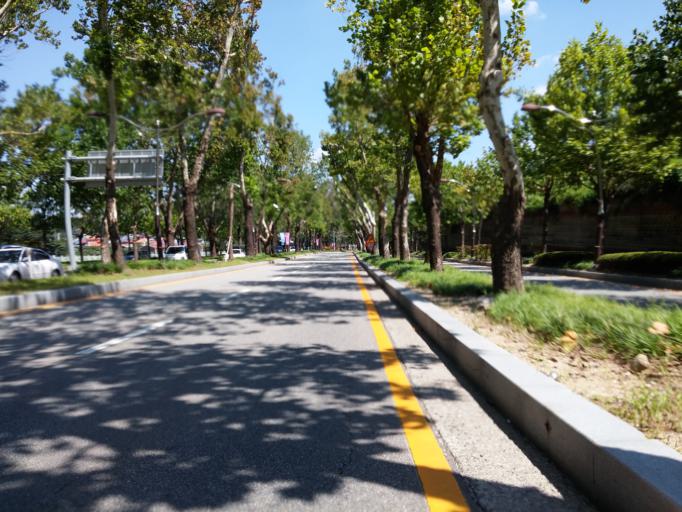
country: KR
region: Chungcheongbuk-do
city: Cheongju-si
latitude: 36.6254
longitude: 127.4120
